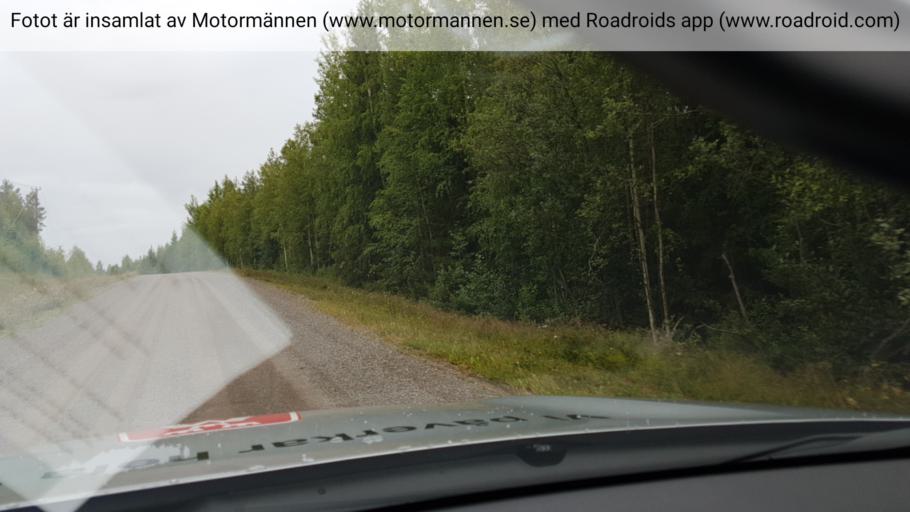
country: SE
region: Norrbotten
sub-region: Alvsbyns Kommun
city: AElvsbyn
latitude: 66.0363
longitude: 20.9914
